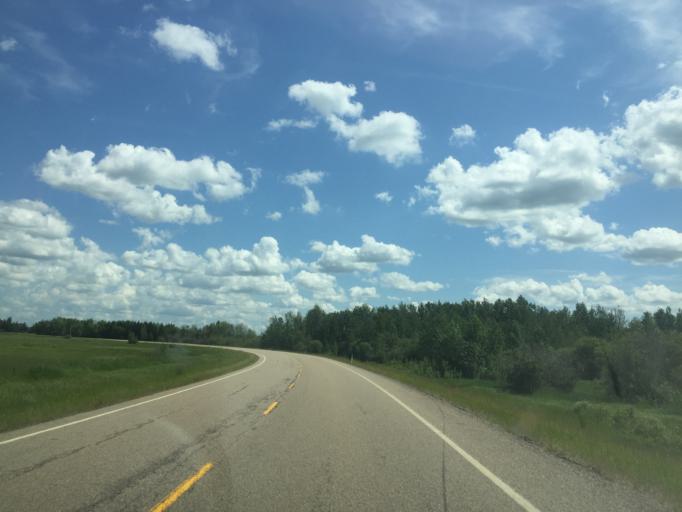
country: CA
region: Alberta
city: Athabasca
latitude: 54.3283
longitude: -113.3227
